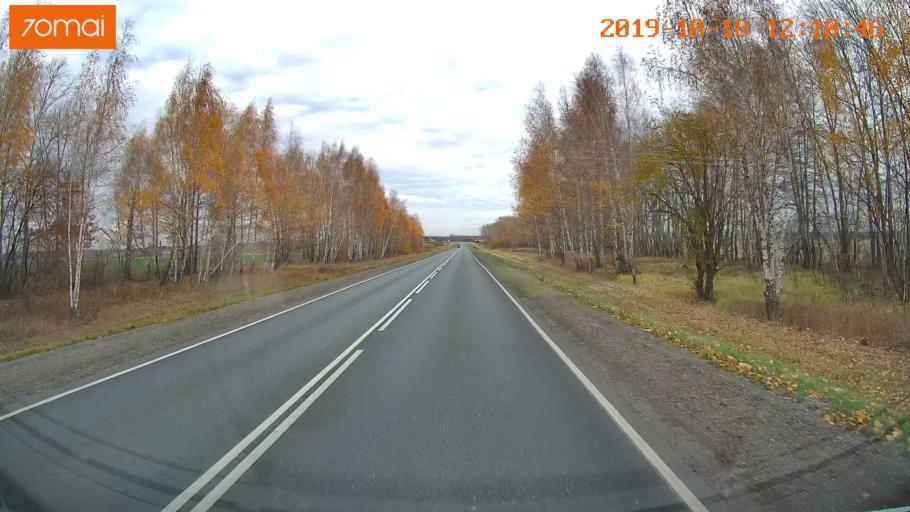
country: RU
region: Rjazan
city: Zakharovo
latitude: 54.3952
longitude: 39.3380
